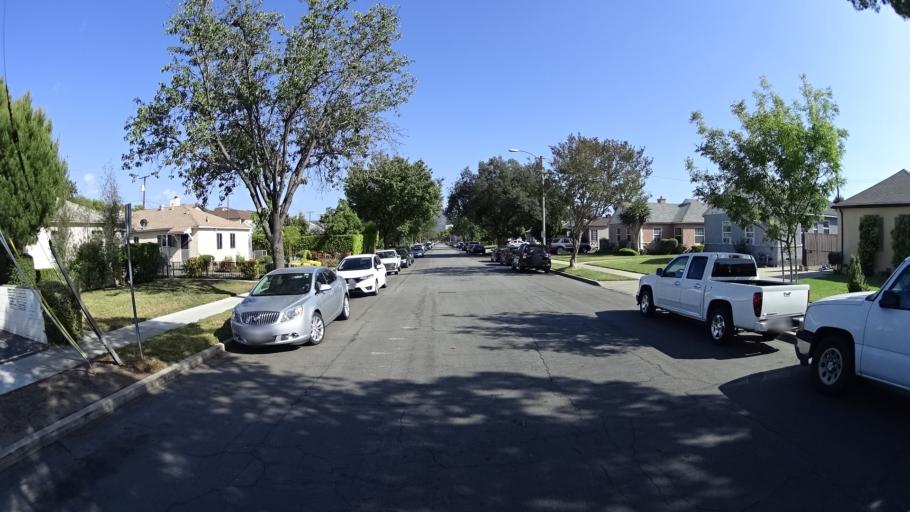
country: US
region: California
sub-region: Los Angeles County
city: North Hollywood
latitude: 34.1739
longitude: -118.3511
